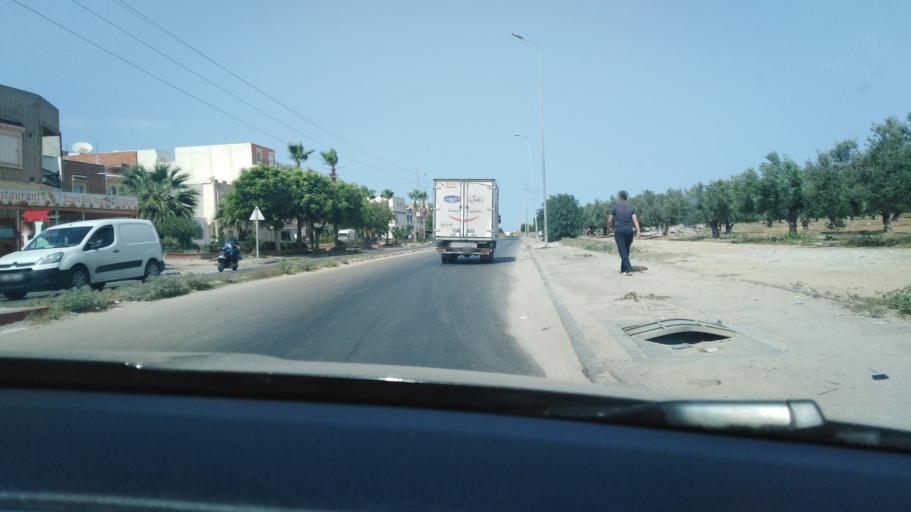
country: TN
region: Susah
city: Masakin
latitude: 35.7891
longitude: 10.5867
